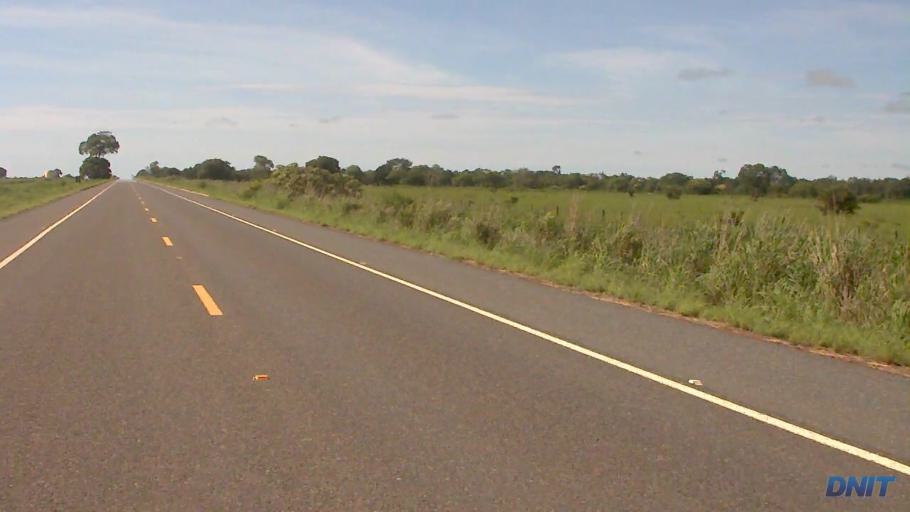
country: BR
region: Goias
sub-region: Sao Miguel Do Araguaia
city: Sao Miguel do Araguaia
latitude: -13.4232
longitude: -50.1286
